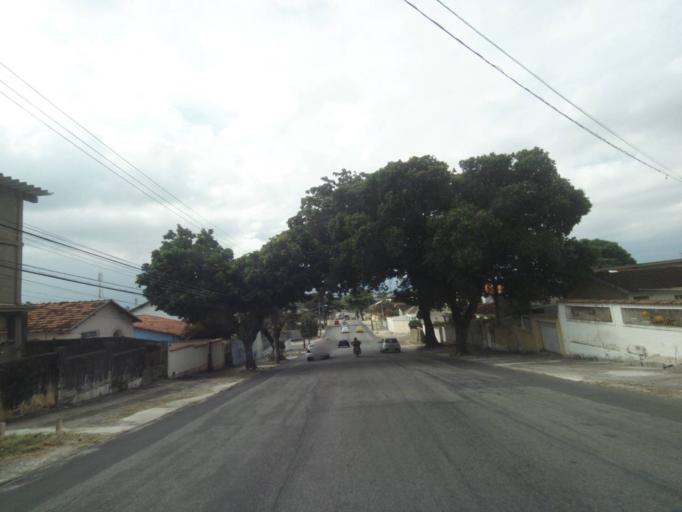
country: BR
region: Rio de Janeiro
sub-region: Nilopolis
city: Nilopolis
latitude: -22.8904
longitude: -43.3908
